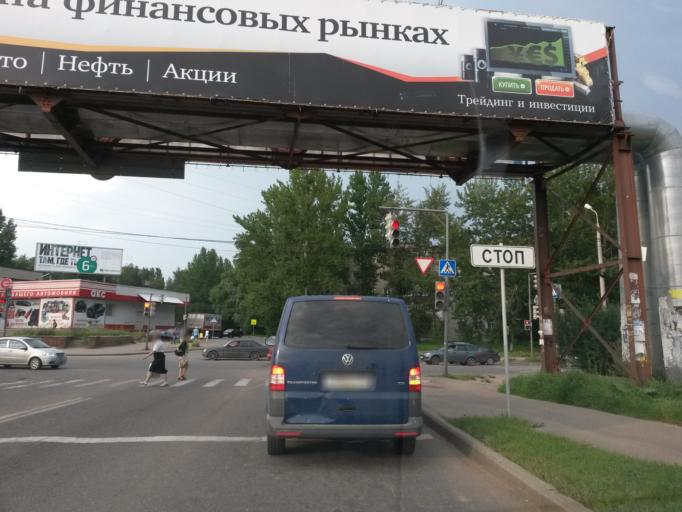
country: RU
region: Jaroslavl
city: Yaroslavl
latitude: 57.5733
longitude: 39.8498
